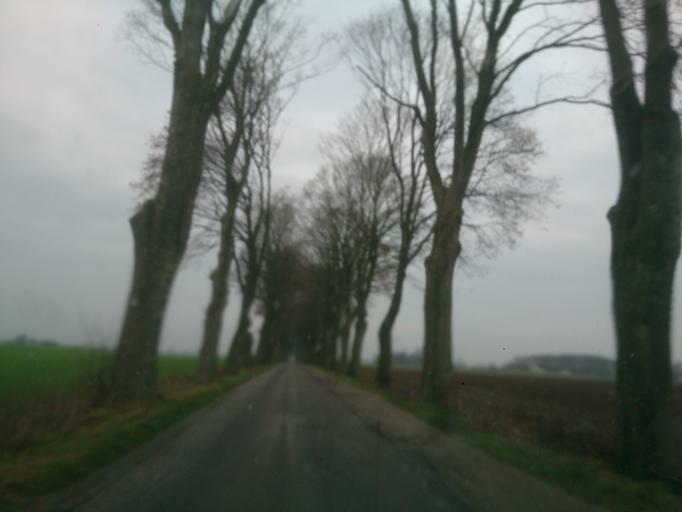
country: PL
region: West Pomeranian Voivodeship
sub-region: Powiat slawienski
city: Slawno
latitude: 54.3160
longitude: 16.6033
